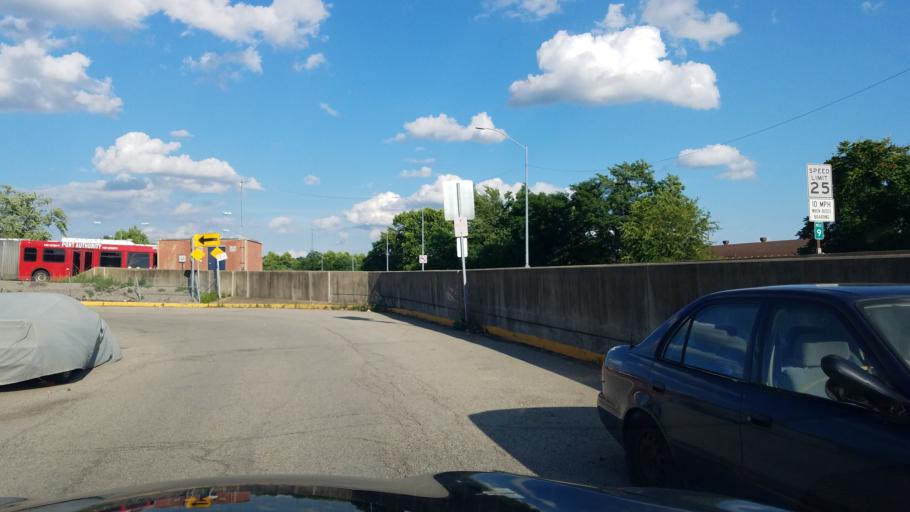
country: US
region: Pennsylvania
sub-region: Allegheny County
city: Rankin
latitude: 40.4153
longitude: -79.8801
